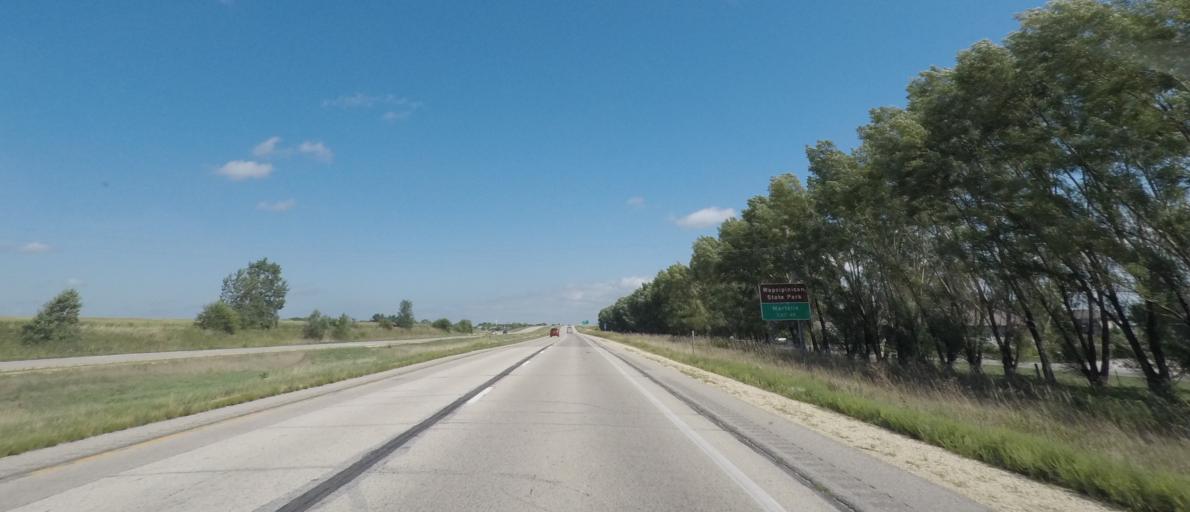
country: US
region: Iowa
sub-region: Jones County
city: Anamosa
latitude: 42.0708
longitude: -91.3465
